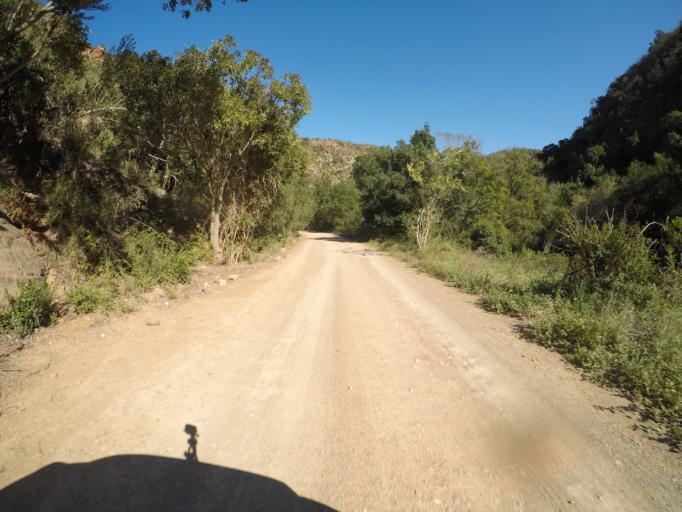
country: ZA
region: Eastern Cape
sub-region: Cacadu District Municipality
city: Kareedouw
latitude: -33.6607
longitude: 24.5371
